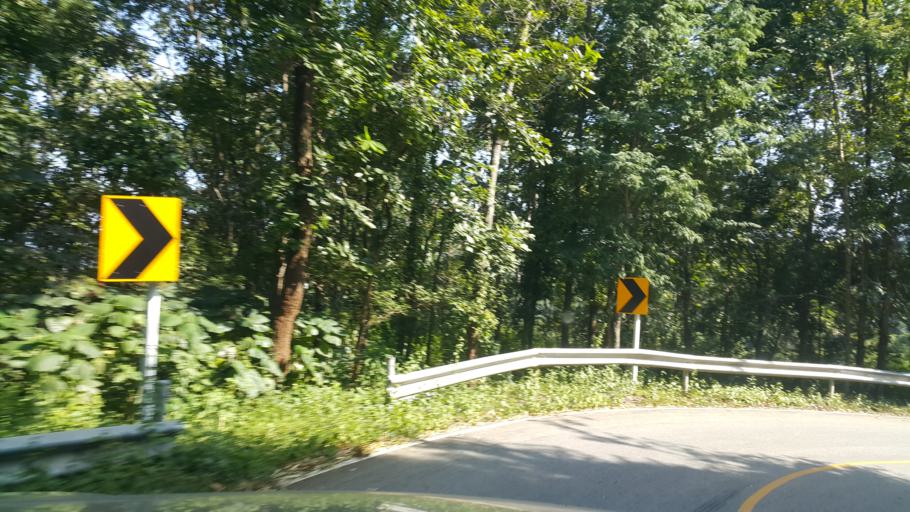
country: TH
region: Chiang Mai
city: Samoeng
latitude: 18.8587
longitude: 98.6730
